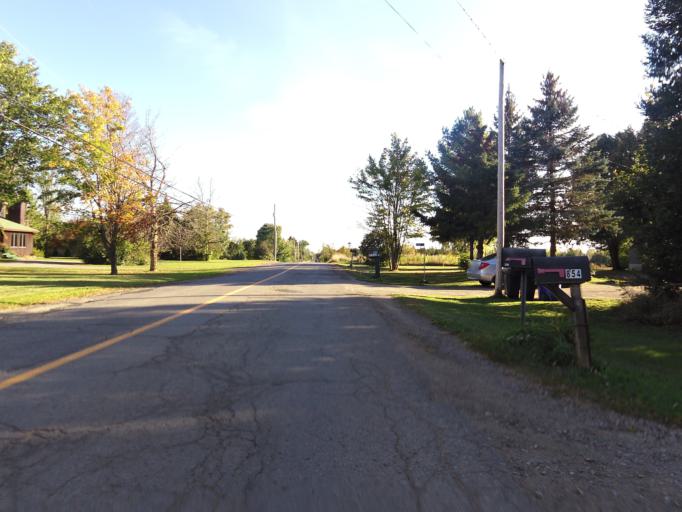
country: CA
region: Ontario
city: Bells Corners
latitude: 45.4344
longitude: -75.8799
